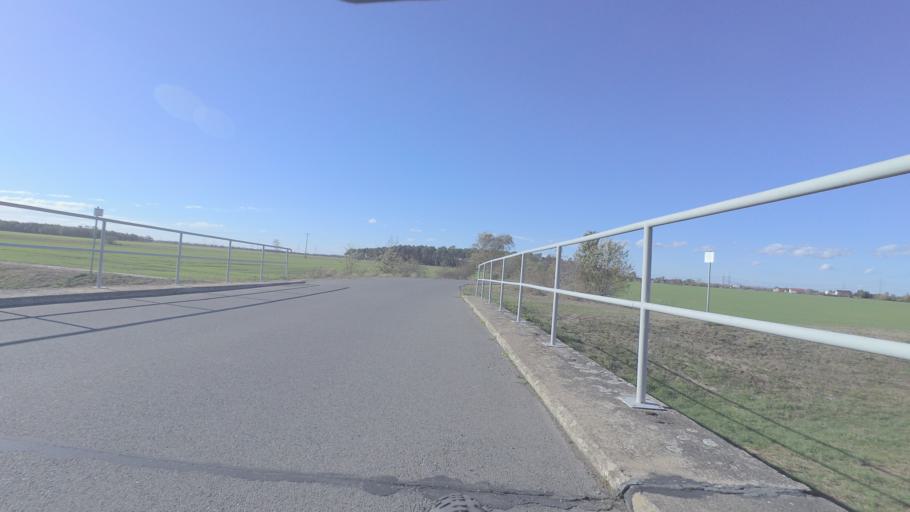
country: DE
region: Saxony
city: Nauwalde
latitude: 51.4443
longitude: 13.4291
